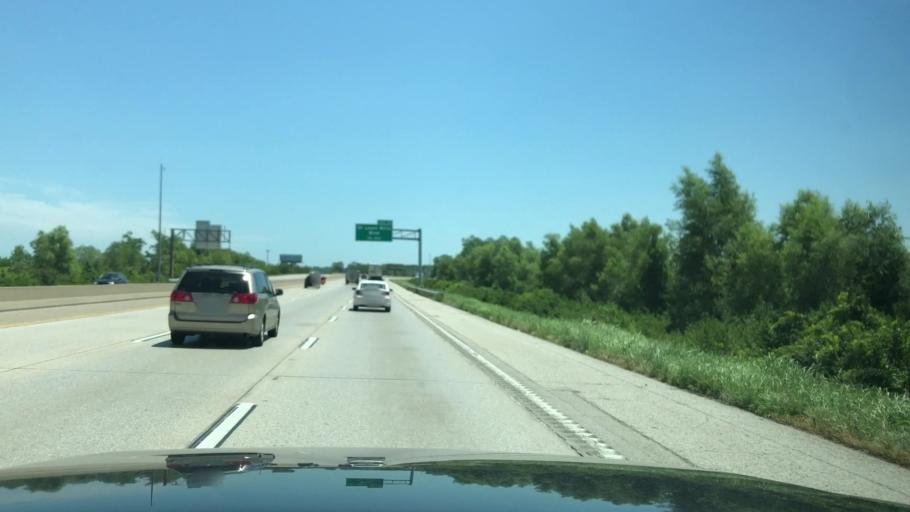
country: US
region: Missouri
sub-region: Saint Louis County
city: Bridgeton
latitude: 38.7902
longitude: -90.4304
